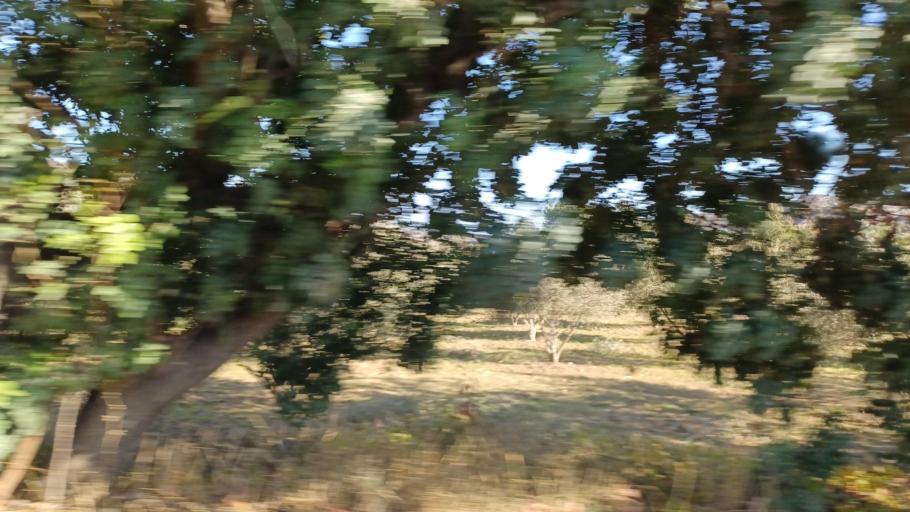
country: CY
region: Limassol
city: Pyrgos
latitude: 34.7790
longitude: 33.2461
